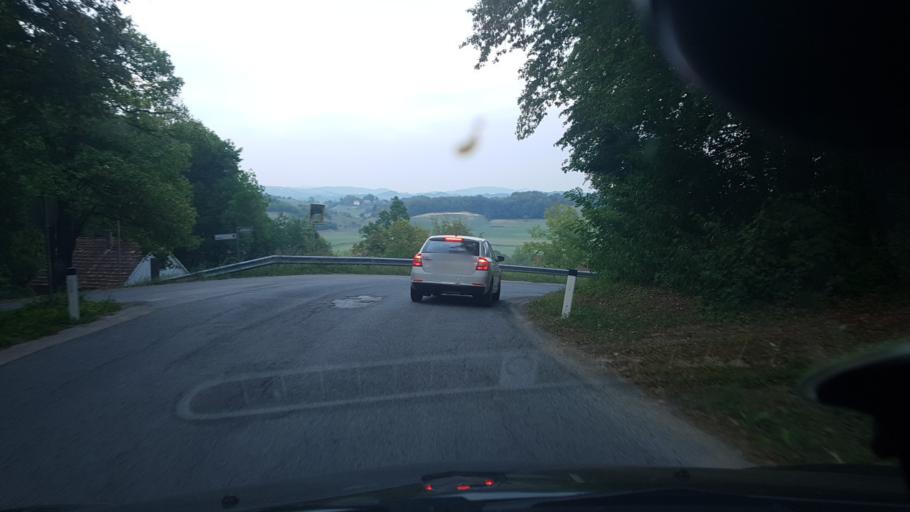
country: SI
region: Kozje
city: Kozje
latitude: 46.1039
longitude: 15.5727
